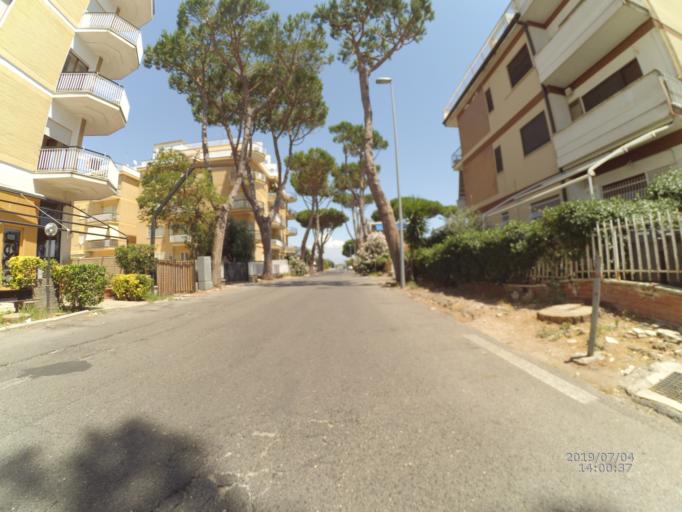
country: IT
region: Latium
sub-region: Provincia di Latina
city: Terracina
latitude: 41.2860
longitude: 13.2192
